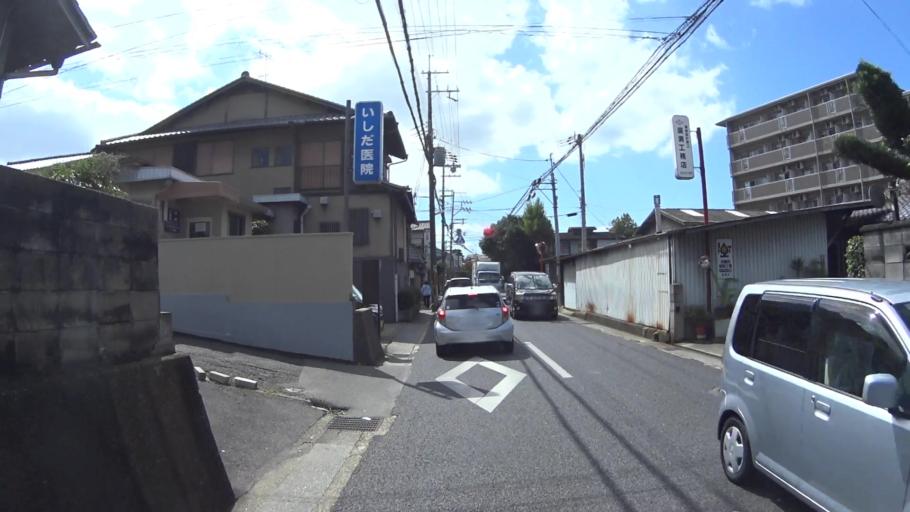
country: JP
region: Kyoto
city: Uji
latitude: 34.9396
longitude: 135.8088
